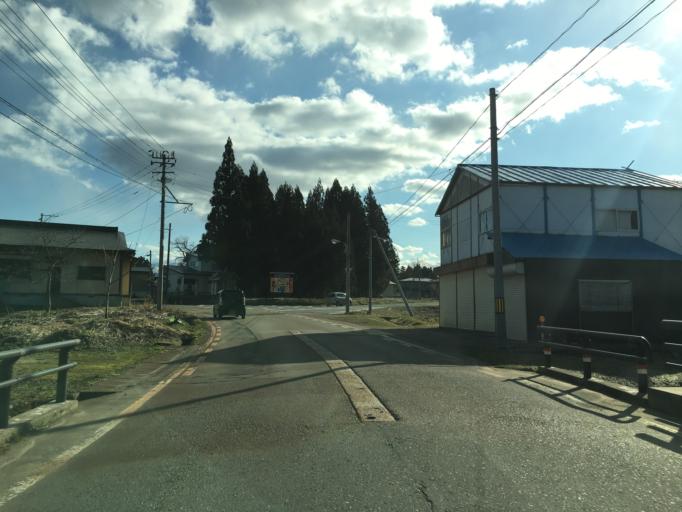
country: JP
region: Yamagata
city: Yonezawa
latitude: 37.9626
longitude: 139.9892
